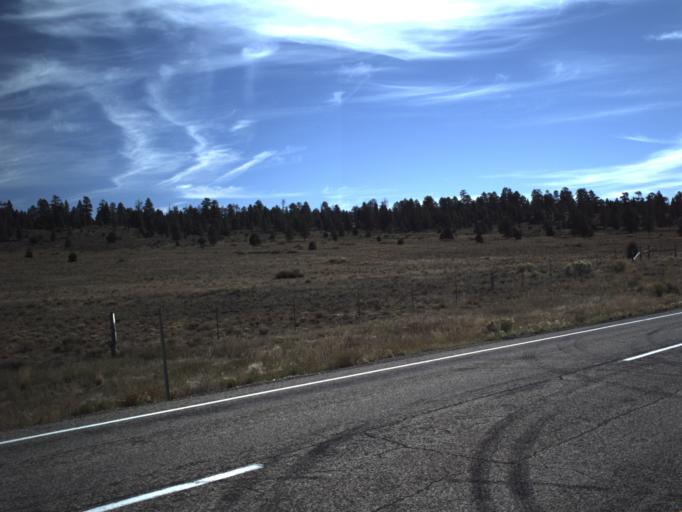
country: US
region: Utah
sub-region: Garfield County
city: Panguitch
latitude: 37.6865
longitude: -112.1378
